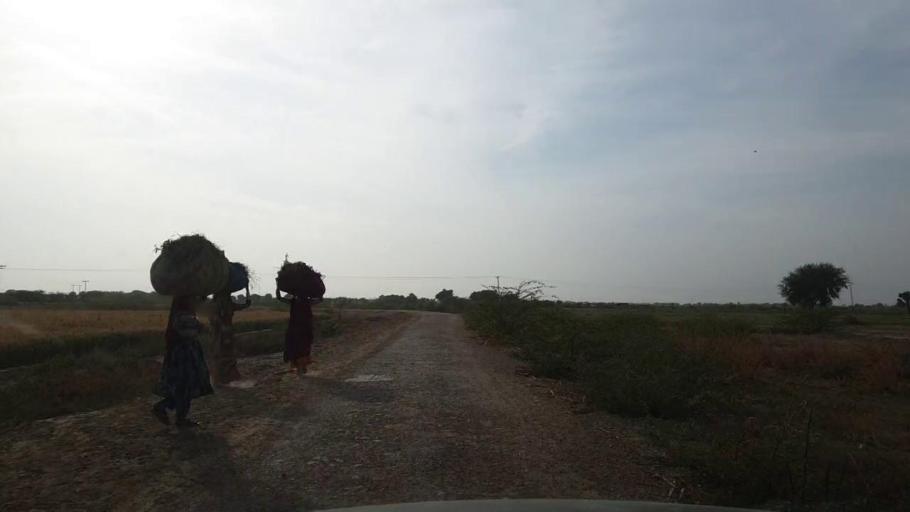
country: PK
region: Sindh
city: Kunri
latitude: 25.1459
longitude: 69.5014
